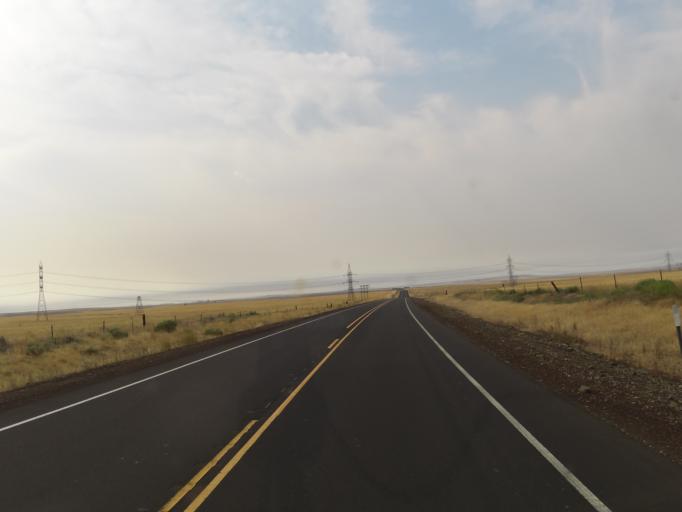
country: US
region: Oregon
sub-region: Sherman County
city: Moro
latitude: 45.2882
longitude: -120.7479
